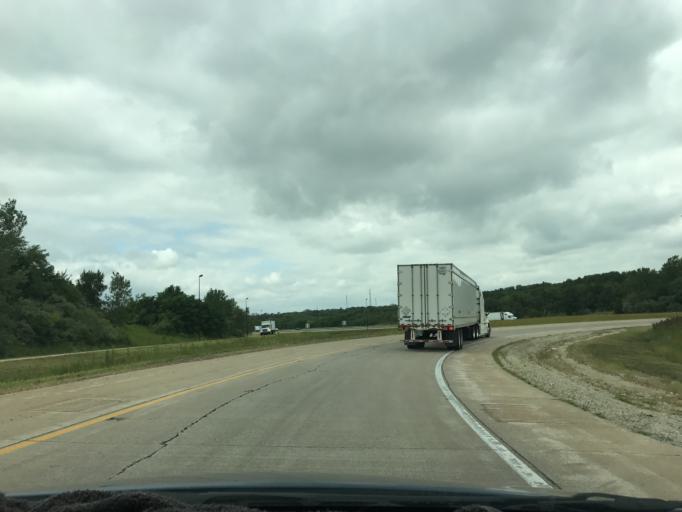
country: US
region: Illinois
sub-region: Henry County
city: Green Rock
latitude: 41.4385
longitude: -90.3316
